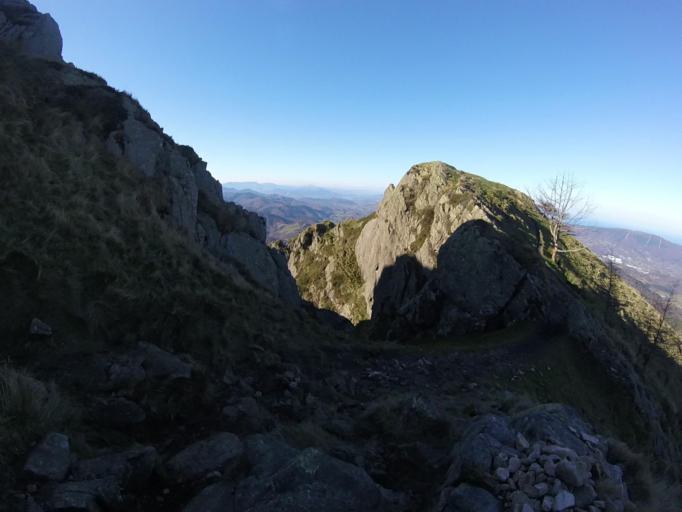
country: ES
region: Basque Country
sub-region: Provincia de Guipuzcoa
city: Irun
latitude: 43.2875
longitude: -1.7838
